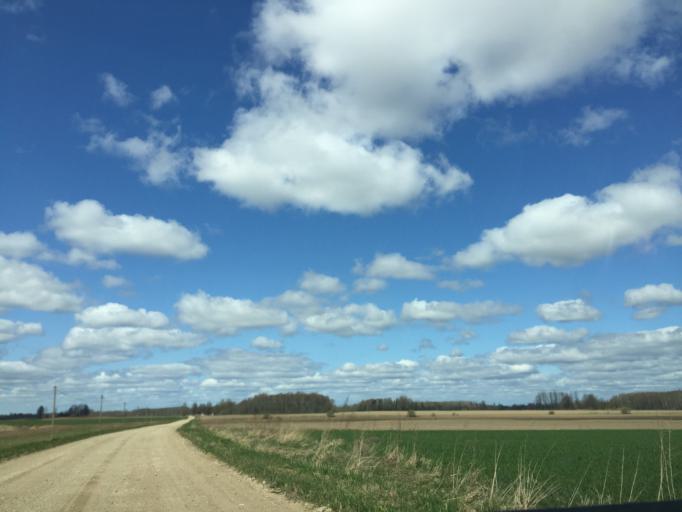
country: LV
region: Vilanu
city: Vilani
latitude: 56.6591
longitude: 27.1184
